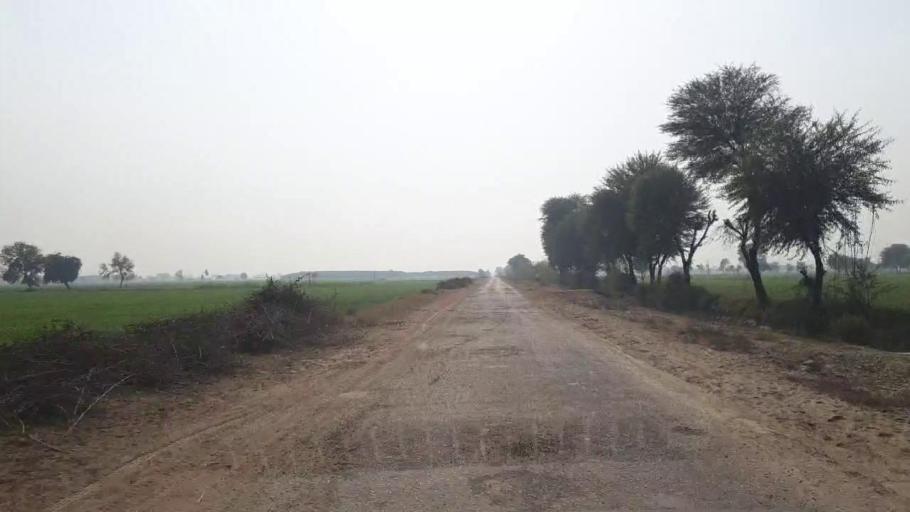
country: PK
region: Sindh
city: Hala
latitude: 25.9219
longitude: 68.4459
